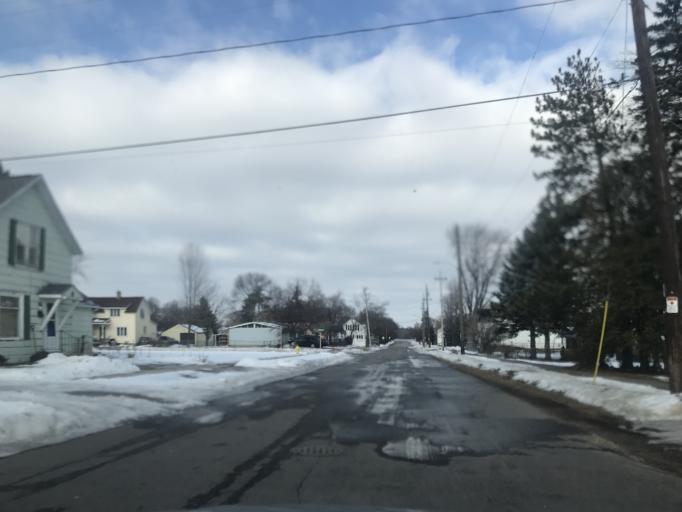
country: US
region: Wisconsin
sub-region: Marinette County
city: Marinette
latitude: 45.1006
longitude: -87.6413
